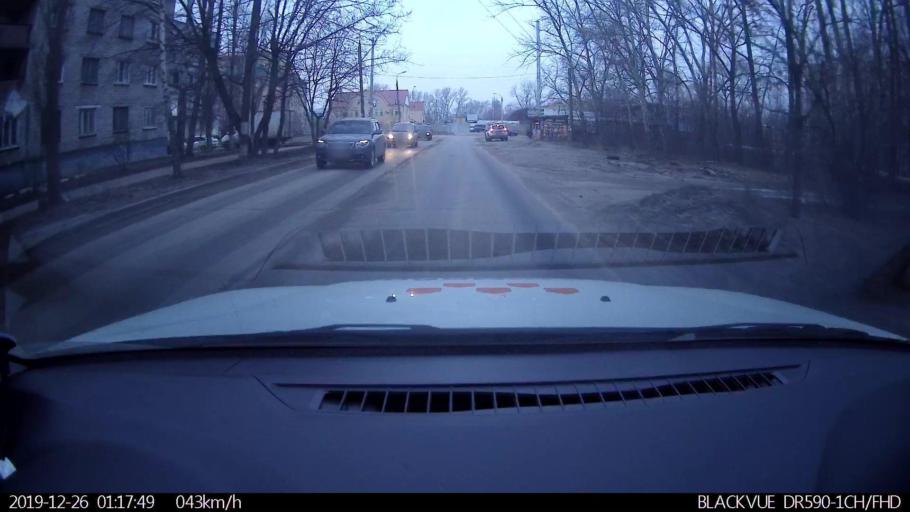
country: RU
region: Nizjnij Novgorod
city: Nizhniy Novgorod
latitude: 56.2697
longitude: 43.8961
